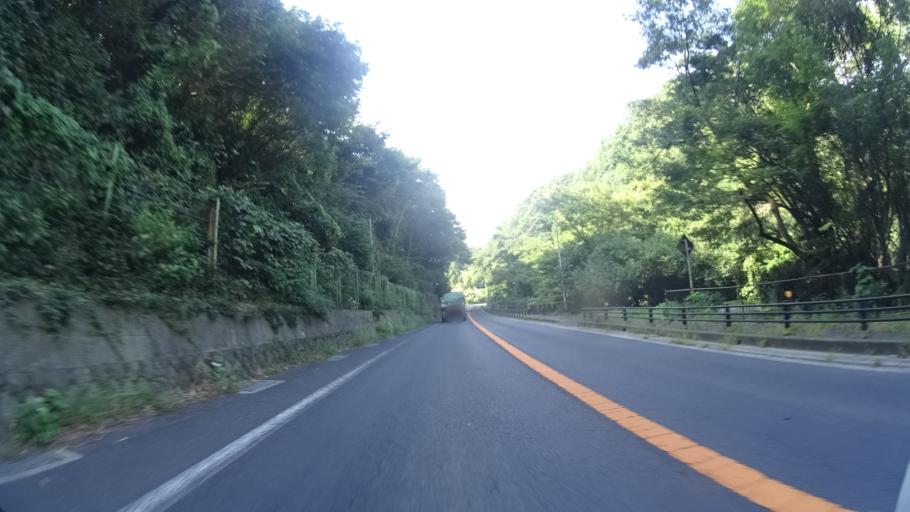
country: JP
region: Shimane
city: Odacho-oda
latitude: 35.2570
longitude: 132.5766
